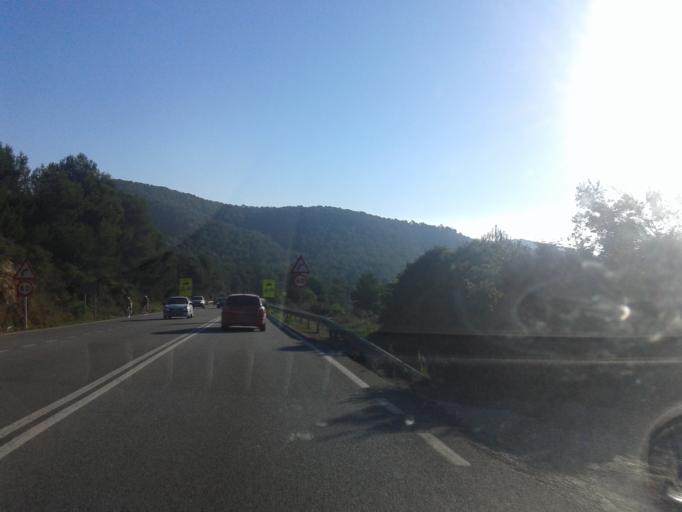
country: ES
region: Catalonia
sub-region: Provincia de Barcelona
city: Vallirana
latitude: 41.3910
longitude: 1.9014
